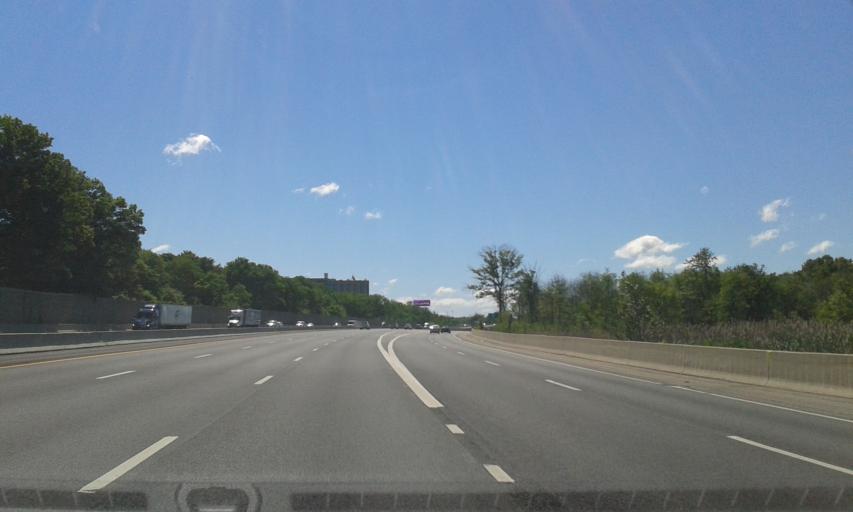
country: US
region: Massachusetts
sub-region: Middlesex County
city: Lowell
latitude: 42.6189
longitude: -71.3360
